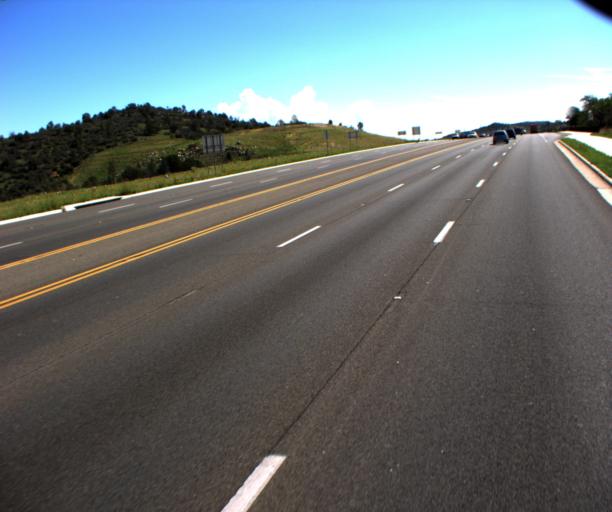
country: US
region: Arizona
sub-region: Yavapai County
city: Prescott
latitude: 34.5487
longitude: -112.4425
